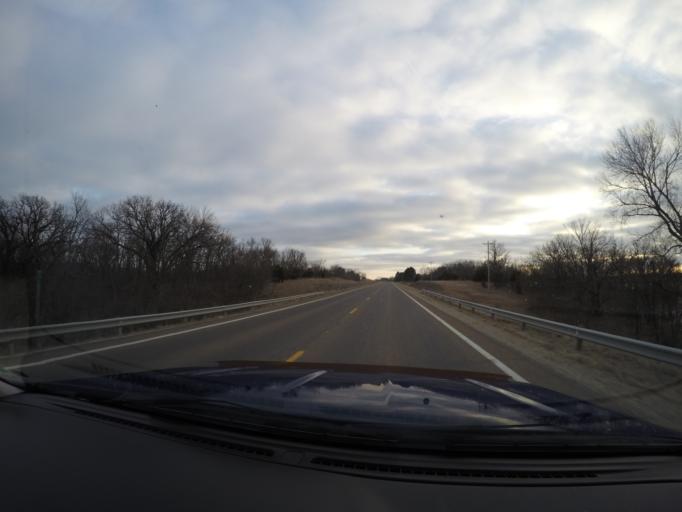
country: US
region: Kansas
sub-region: Morris County
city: Council Grove
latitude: 38.7049
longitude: -96.4972
